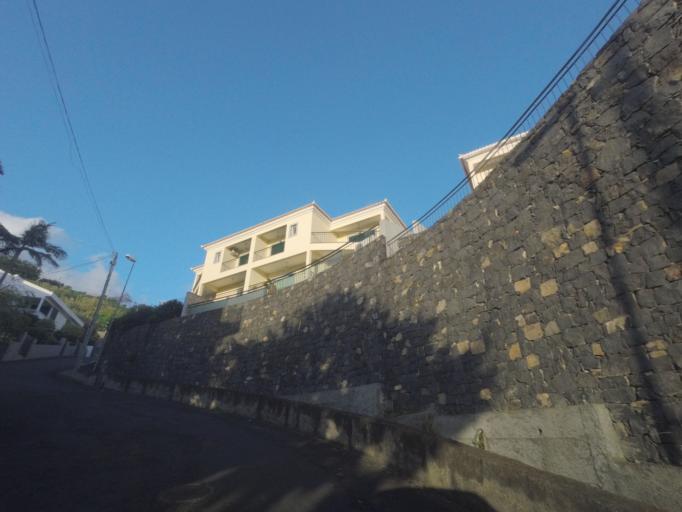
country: PT
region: Madeira
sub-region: Funchal
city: Nossa Senhora do Monte
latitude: 32.6568
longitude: -16.8913
